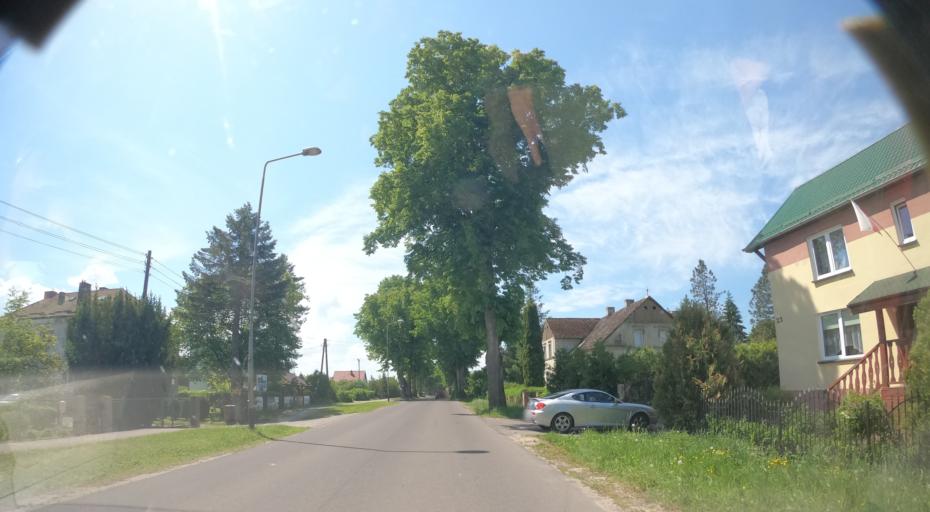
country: PL
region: West Pomeranian Voivodeship
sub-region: Powiat kolobrzeski
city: Dygowo
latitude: 54.1383
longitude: 15.7297
